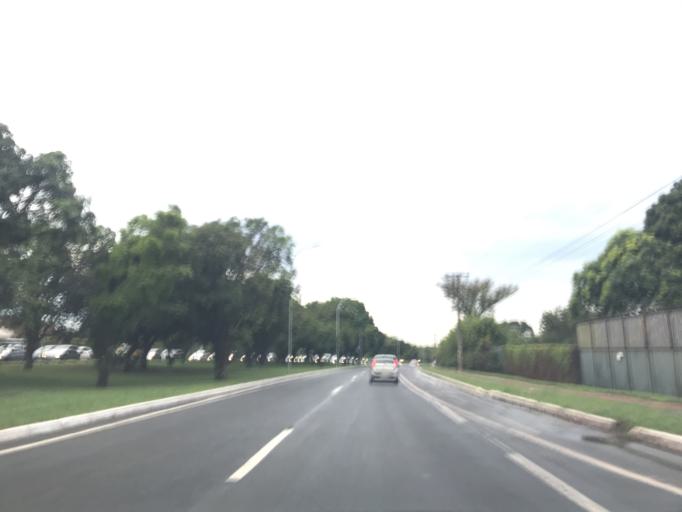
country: BR
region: Federal District
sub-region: Brasilia
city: Brasilia
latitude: -15.8491
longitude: -47.8751
